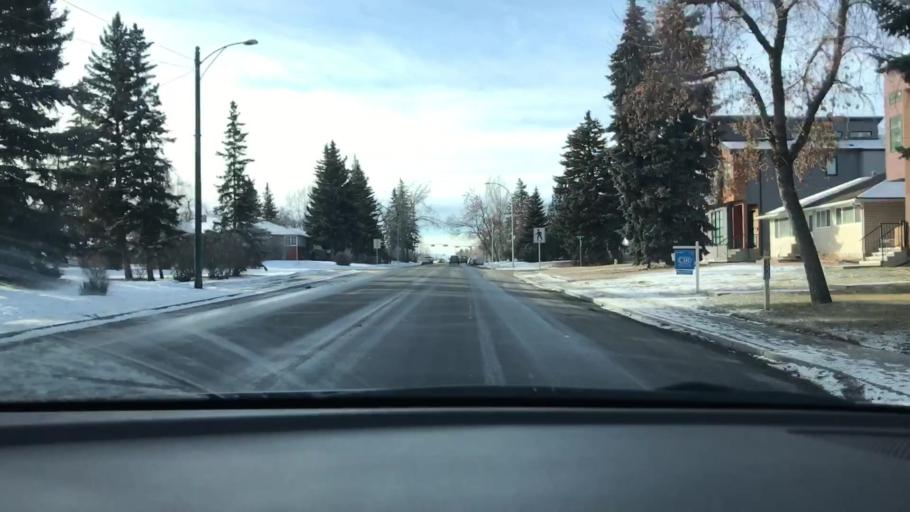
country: CA
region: Alberta
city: Calgary
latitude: 51.0237
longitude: -114.1373
